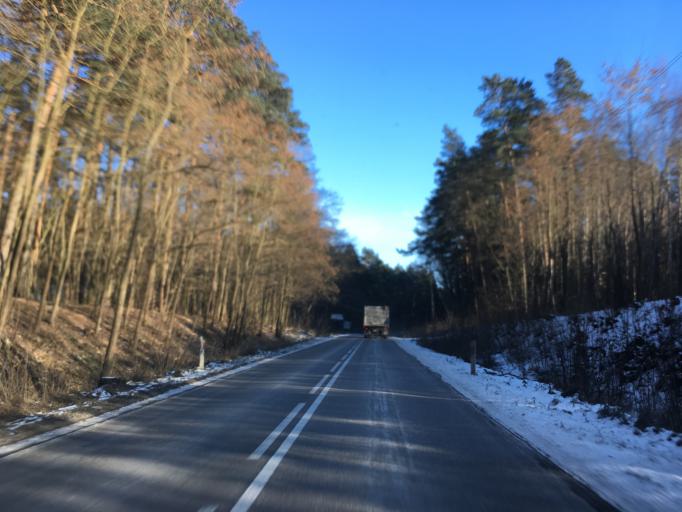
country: PL
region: Pomeranian Voivodeship
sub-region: Powiat starogardzki
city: Lubichowo
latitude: 53.8780
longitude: 18.3689
